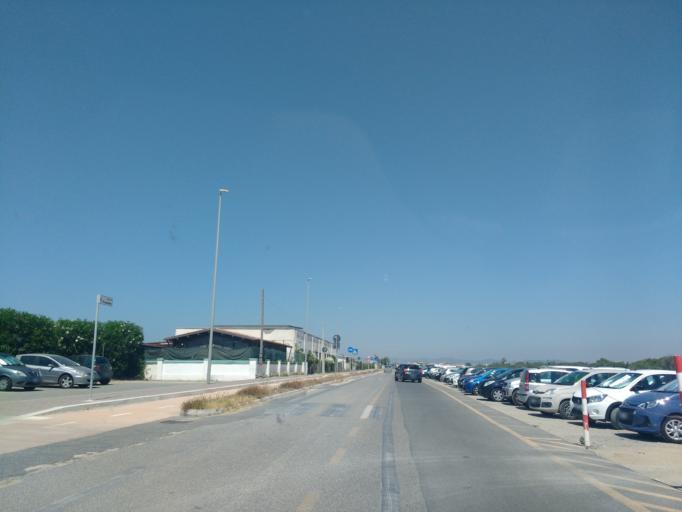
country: IT
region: Latium
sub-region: Citta metropolitana di Roma Capitale
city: Passo Oscuro
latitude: 41.8880
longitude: 12.1687
